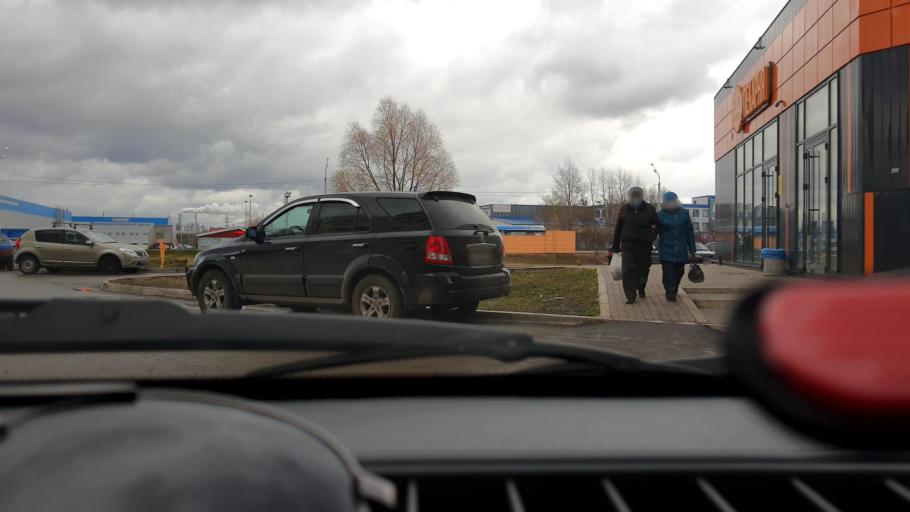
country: RU
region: Bashkortostan
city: Iglino
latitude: 54.7556
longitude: 56.2476
